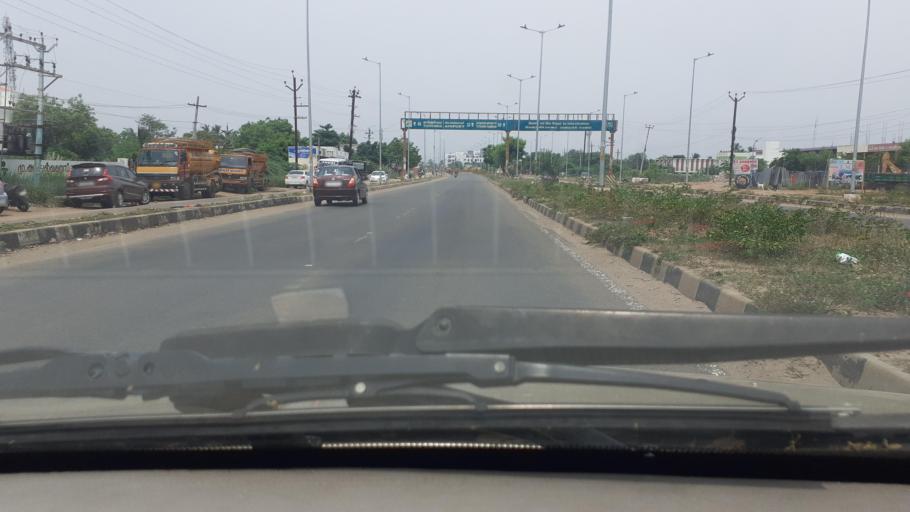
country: IN
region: Tamil Nadu
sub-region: Tirunelveli Kattabo
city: Tirunelveli
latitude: 8.7144
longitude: 77.7679
